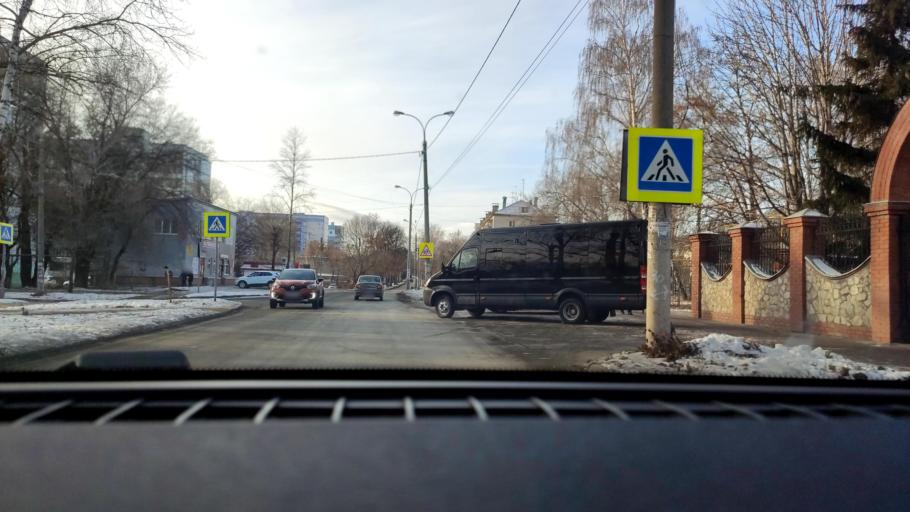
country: RU
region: Samara
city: Petra-Dubrava
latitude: 53.3028
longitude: 50.2790
